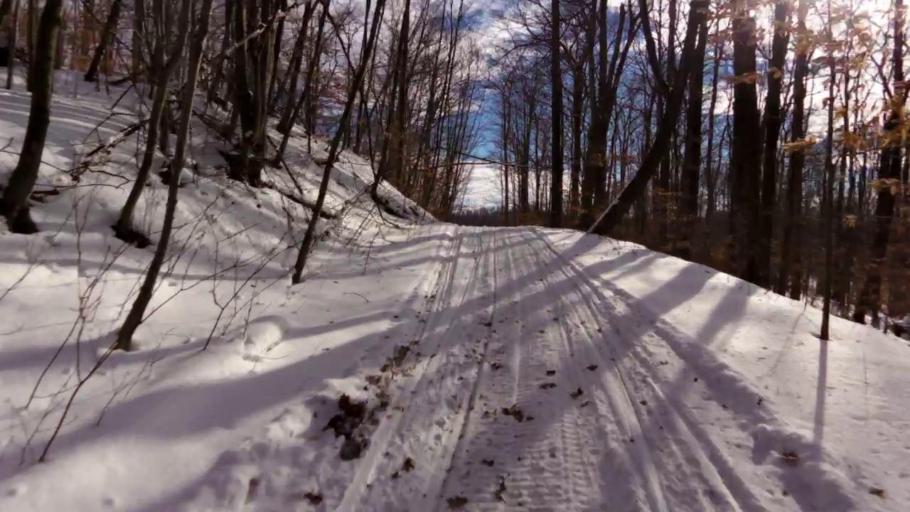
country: US
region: Pennsylvania
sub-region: McKean County
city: Foster Brook
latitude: 42.0067
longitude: -78.5948
